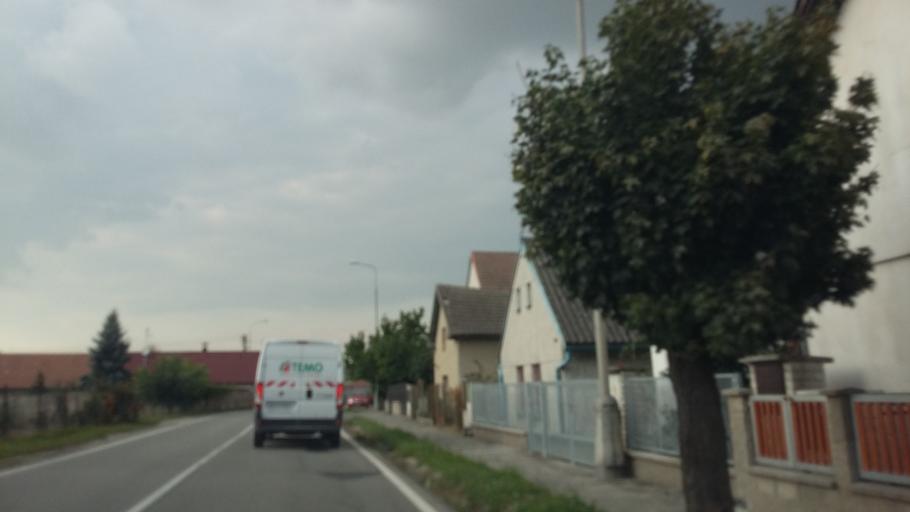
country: CZ
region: Central Bohemia
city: Benatky nad Jizerou
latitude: 50.3294
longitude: 14.8656
